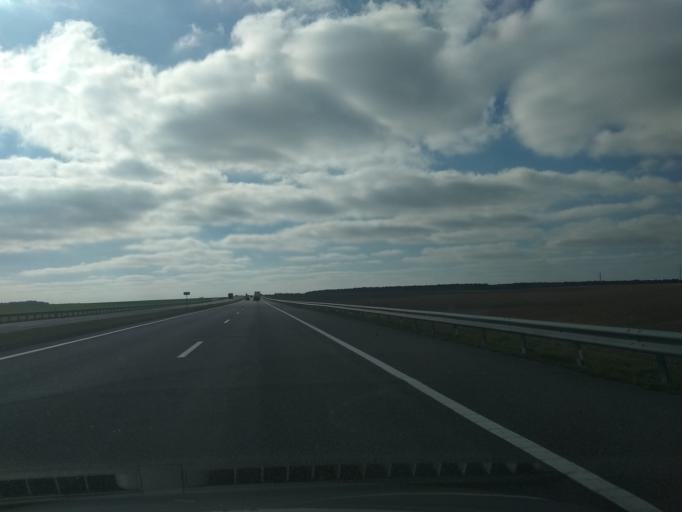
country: BY
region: Grodnenskaya
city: Mir
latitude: 53.4315
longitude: 26.5845
